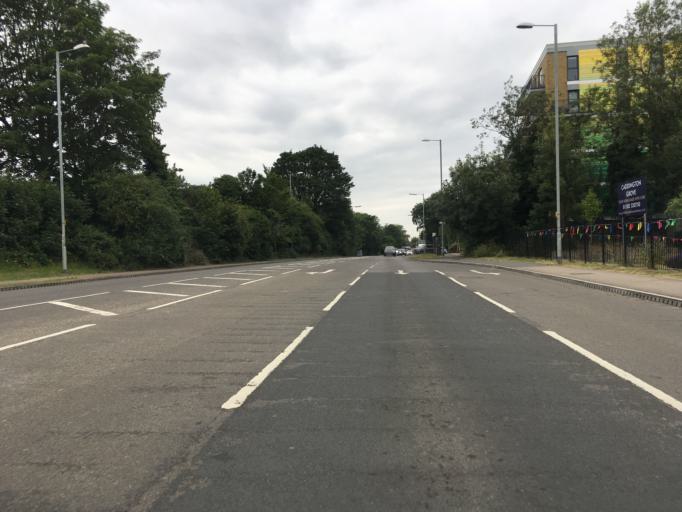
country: GB
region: England
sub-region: Central Bedfordshire
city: Kensworth
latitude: 51.8737
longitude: -0.5021
